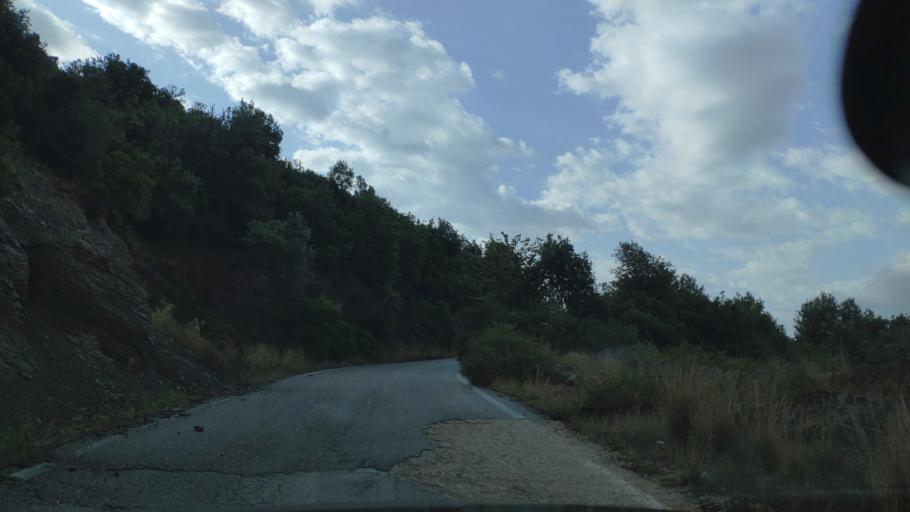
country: GR
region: West Greece
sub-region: Nomos Aitolias kai Akarnanias
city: Sardinia
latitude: 38.8889
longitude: 21.2405
